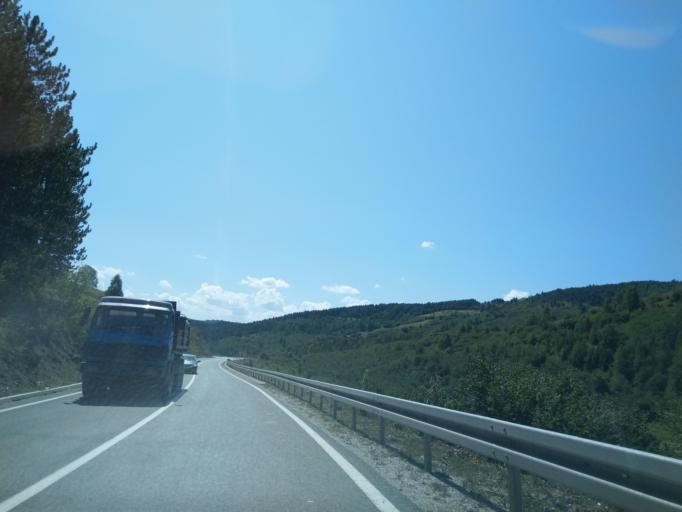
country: RS
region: Central Serbia
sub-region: Zlatiborski Okrug
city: Sjenica
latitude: 43.2886
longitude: 19.9426
